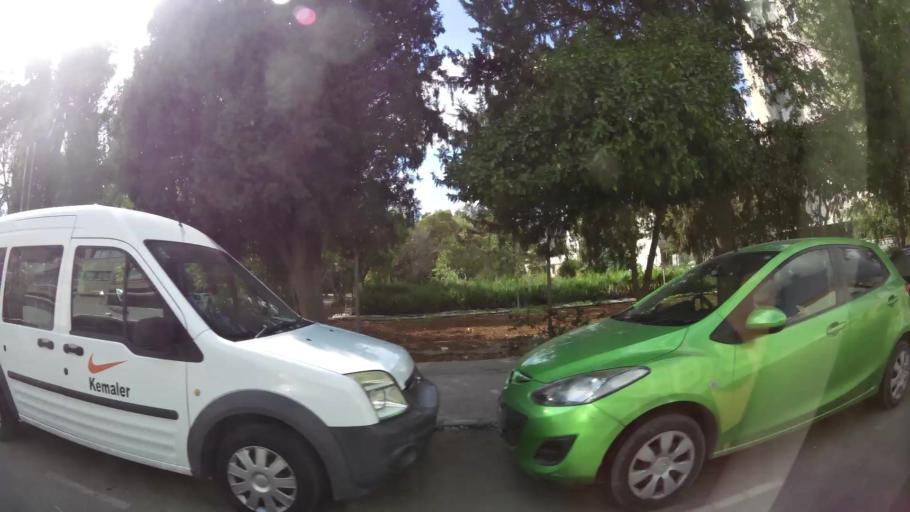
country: CY
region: Lefkosia
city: Nicosia
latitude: 35.1840
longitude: 33.3512
